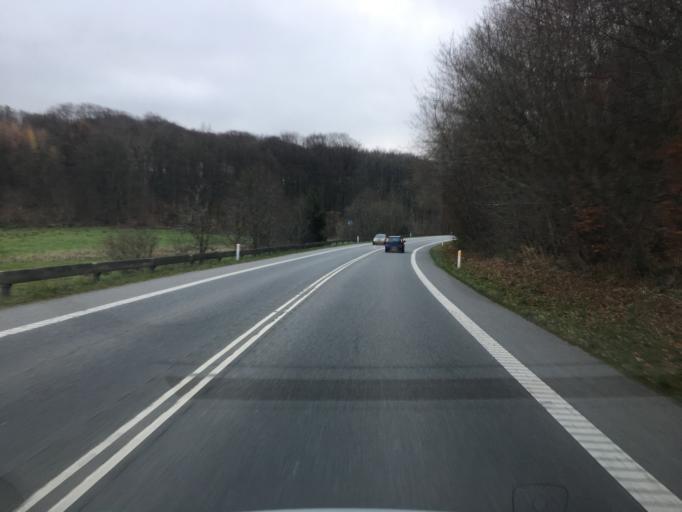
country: DK
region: South Denmark
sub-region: Aabenraa Kommune
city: Aabenraa
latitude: 55.0296
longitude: 9.3774
